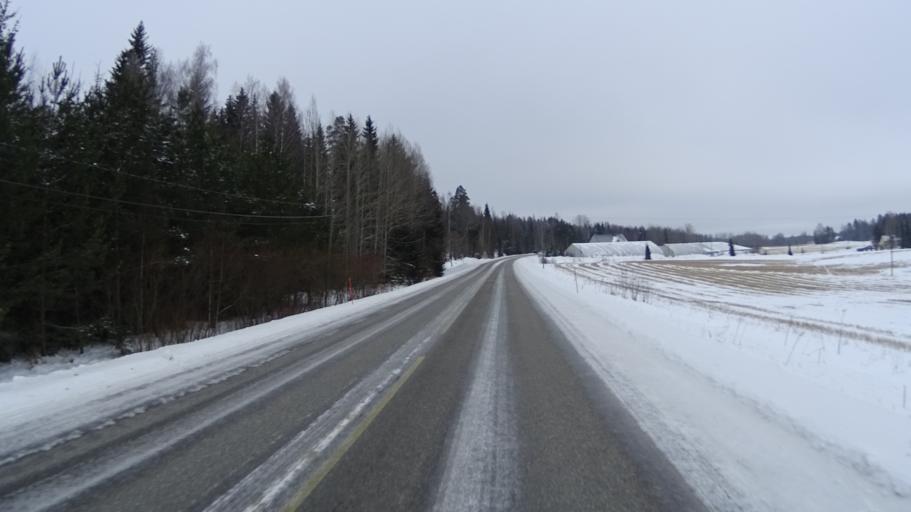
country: FI
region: Uusimaa
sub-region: Helsinki
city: Karkkila
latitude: 60.5150
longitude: 24.1758
